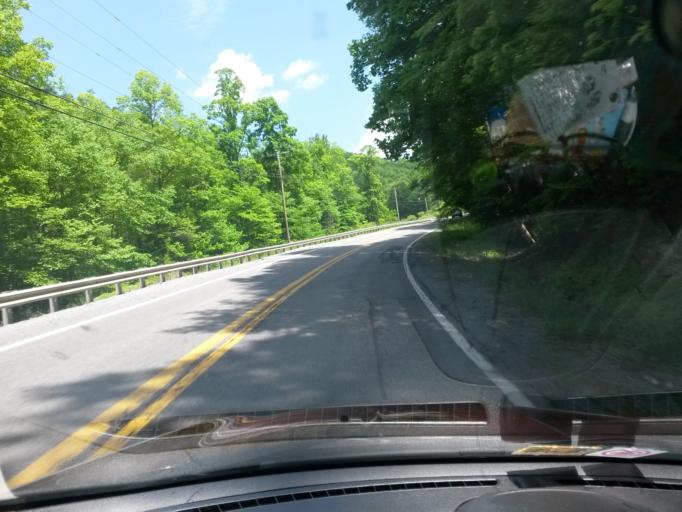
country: US
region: West Virginia
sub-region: McDowell County
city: Welch
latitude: 37.4815
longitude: -81.5458
